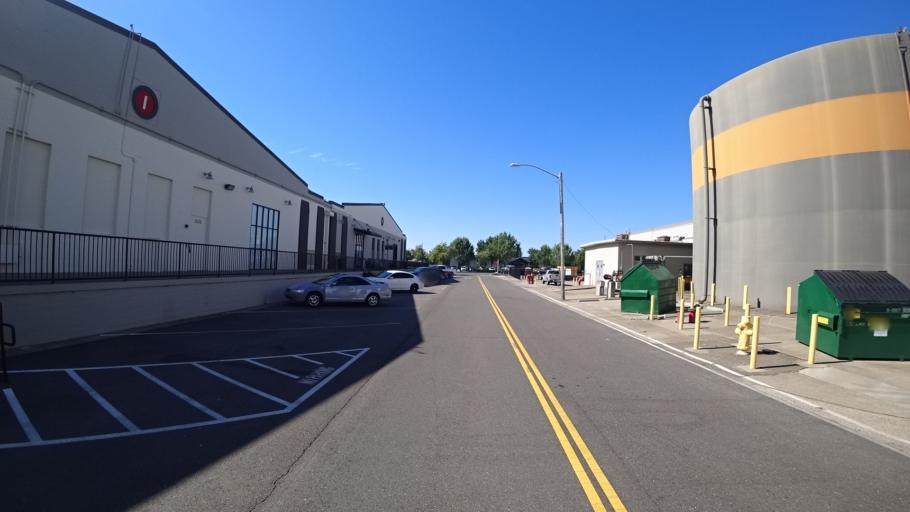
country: US
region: California
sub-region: Sacramento County
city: North Highlands
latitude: 38.6586
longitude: -121.3901
